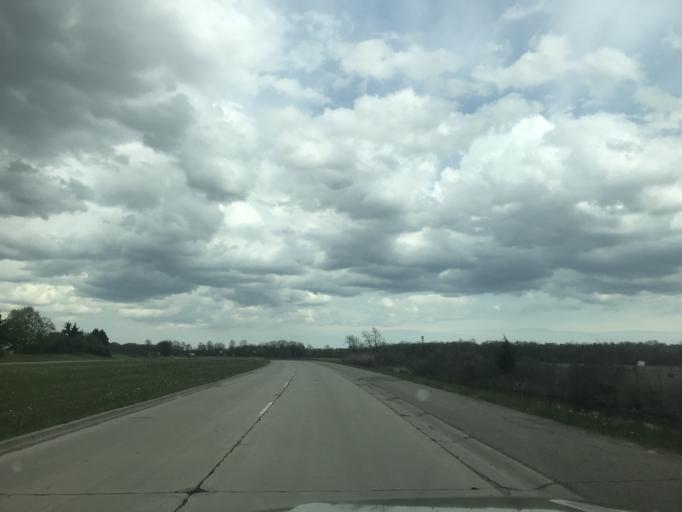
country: US
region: Michigan
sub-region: Wayne County
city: Romulus
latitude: 42.1914
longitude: -83.3603
